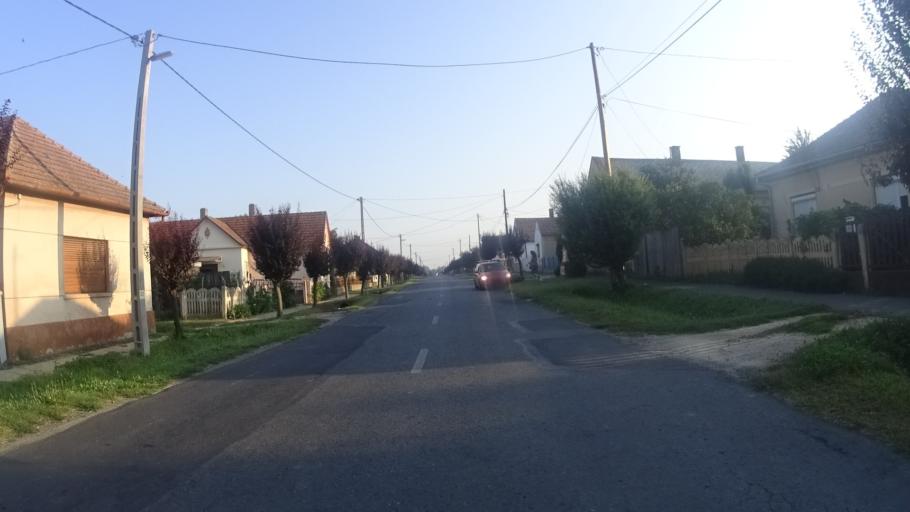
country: HU
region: Zala
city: Zalakomar
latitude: 46.5536
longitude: 17.1747
